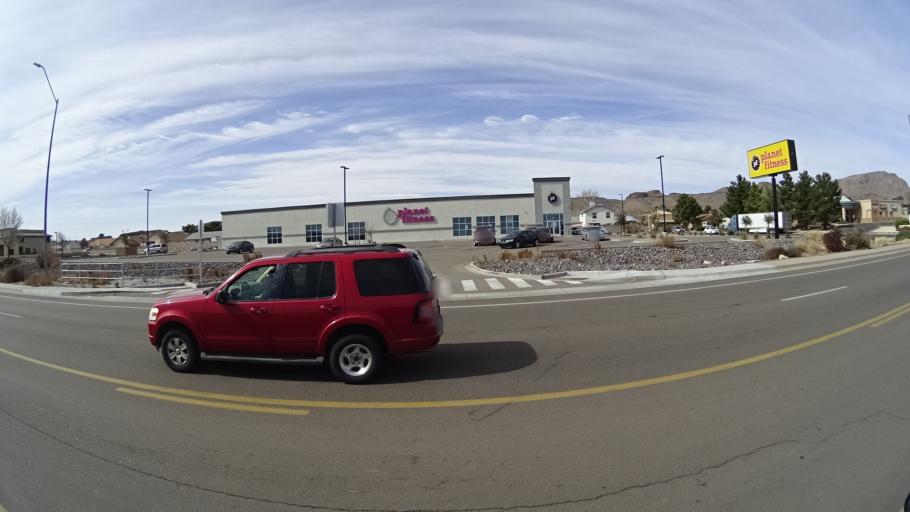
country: US
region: Arizona
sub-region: Mohave County
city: New Kingman-Butler
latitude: 35.2359
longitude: -114.0374
